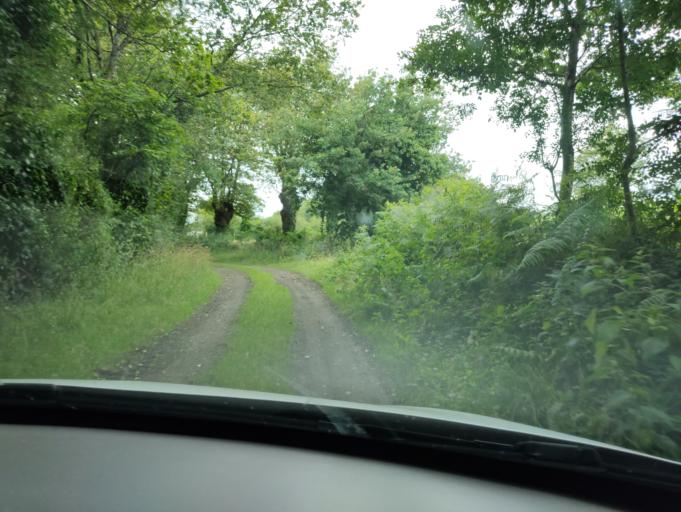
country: FR
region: Pays de la Loire
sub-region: Departement de la Loire-Atlantique
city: Chateaubriant
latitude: 47.7019
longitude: -1.4231
